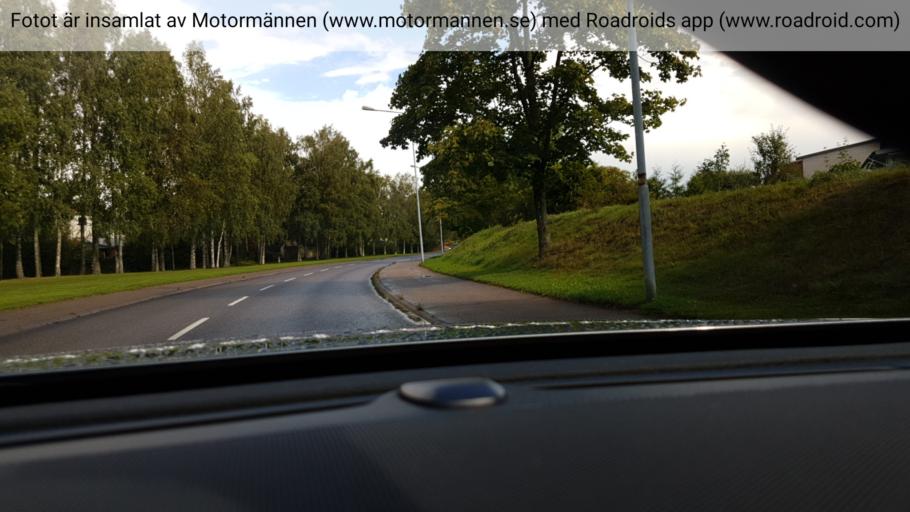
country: SE
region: Vaestra Goetaland
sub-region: Vanersborgs Kommun
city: Vanersborg
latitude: 58.3701
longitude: 12.2847
